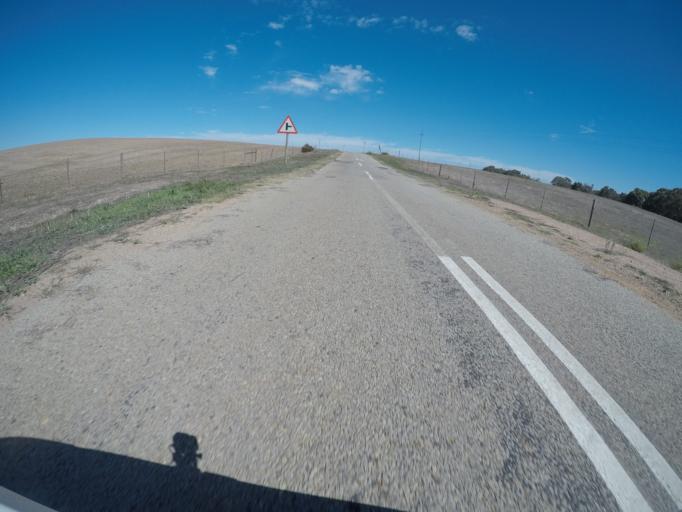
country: ZA
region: Western Cape
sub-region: City of Cape Town
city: Atlantis
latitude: -33.6182
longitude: 18.6333
